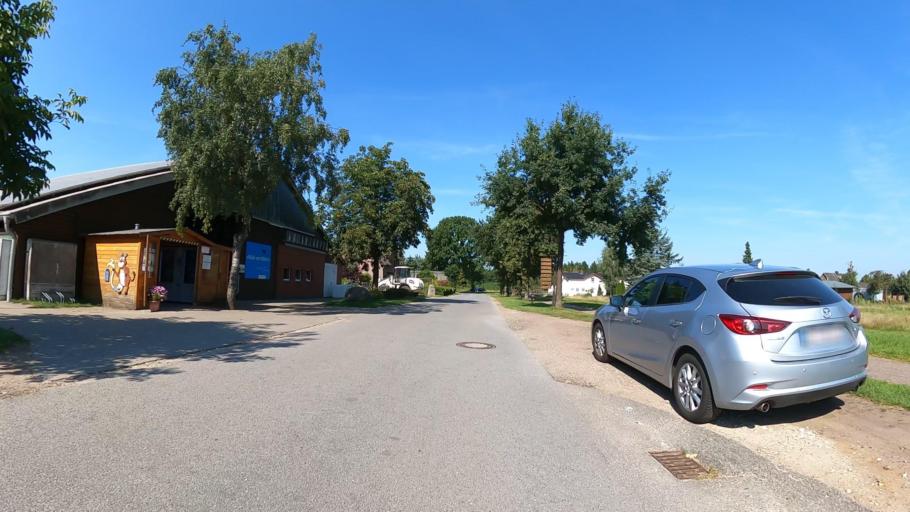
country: DE
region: Schleswig-Holstein
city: Nutzen
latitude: 53.8640
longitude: 9.9163
